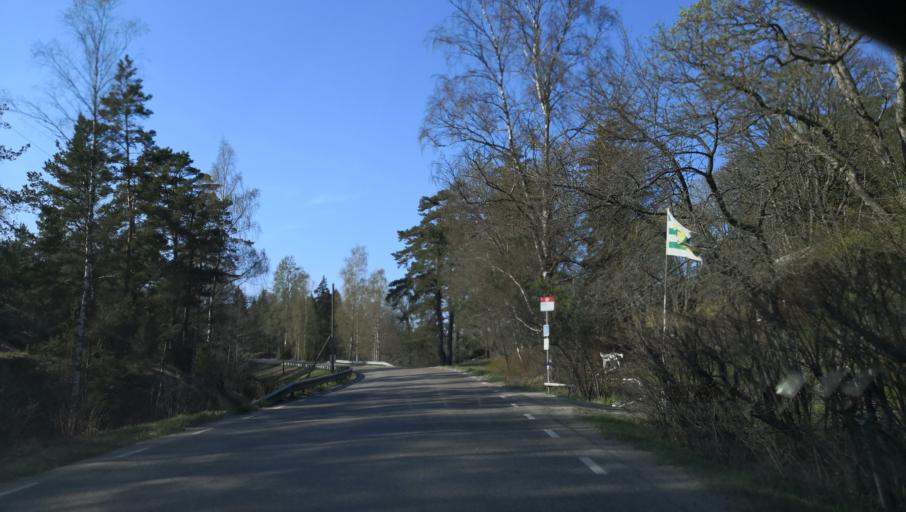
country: SE
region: Stockholm
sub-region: Varmdo Kommun
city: Holo
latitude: 59.3075
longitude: 18.5862
